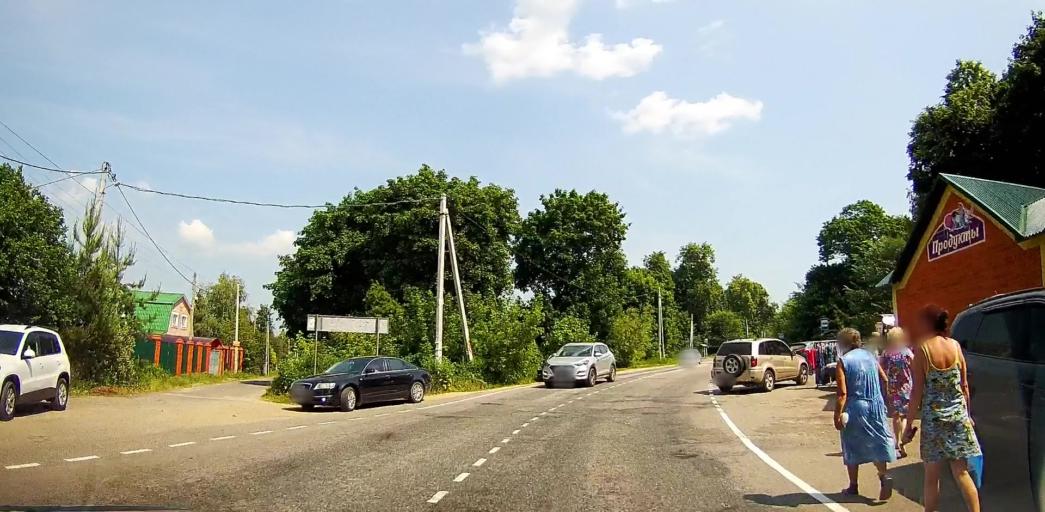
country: RU
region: Moskovskaya
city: Meshcherino
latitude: 55.2441
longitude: 38.3168
